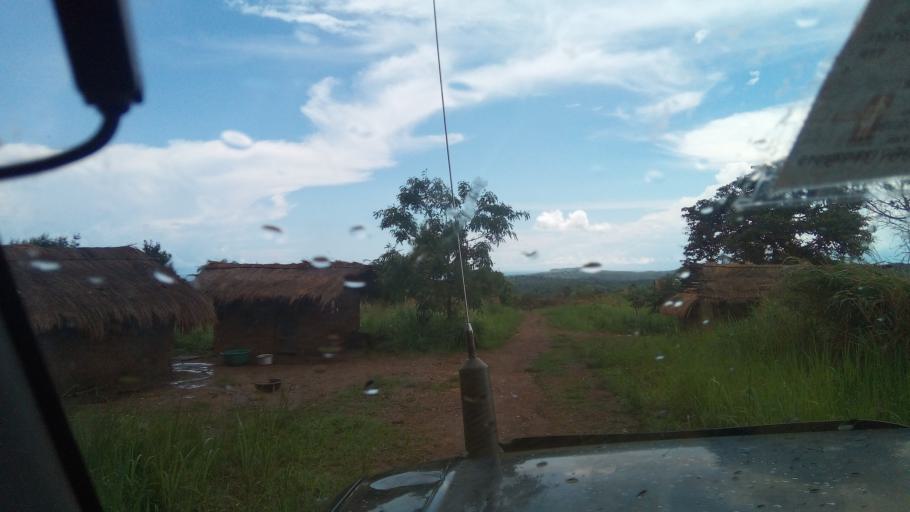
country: CD
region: Katanga
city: Kalemie
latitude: -5.7171
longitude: 29.3026
